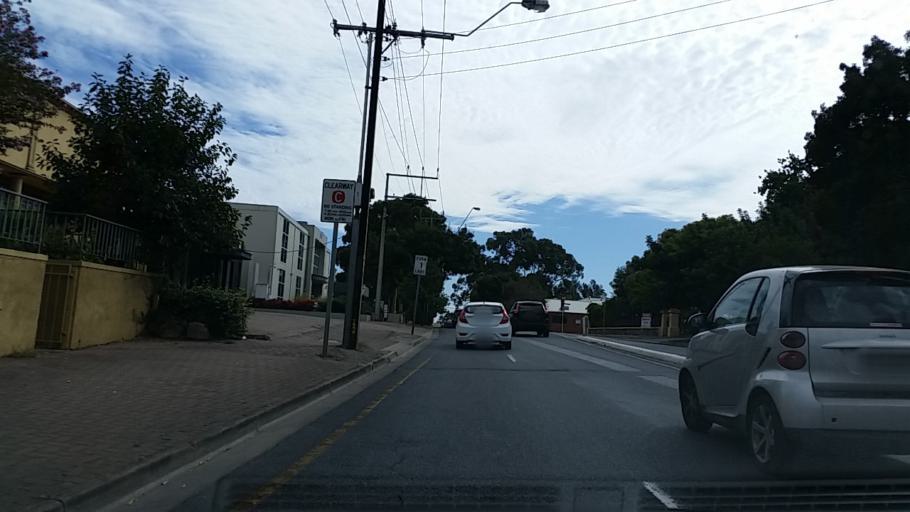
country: AU
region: South Australia
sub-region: Norwood Payneham St Peters
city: Trinity Gardens
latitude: -34.9213
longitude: 138.6231
